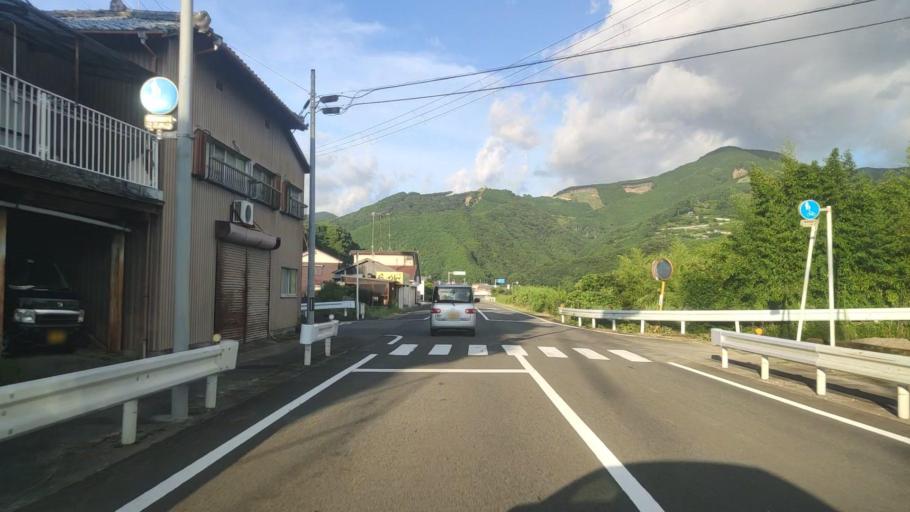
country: JP
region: Wakayama
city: Tanabe
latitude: 33.7185
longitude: 135.4742
